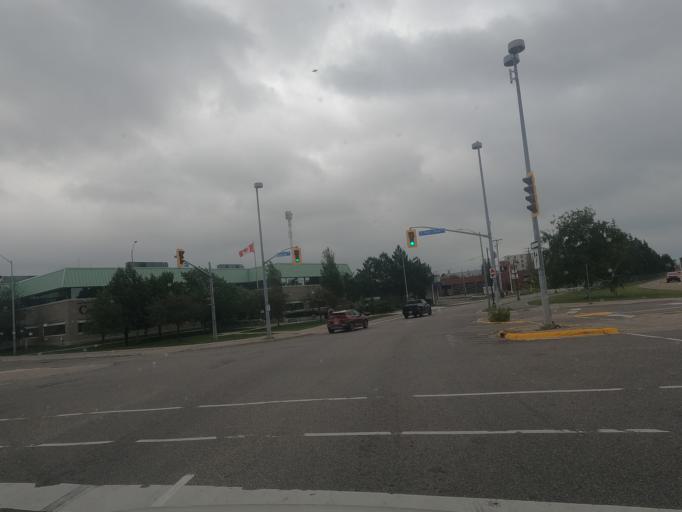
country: CA
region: Ontario
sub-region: Algoma
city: Sault Ste. Marie
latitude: 46.5165
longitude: -84.3425
